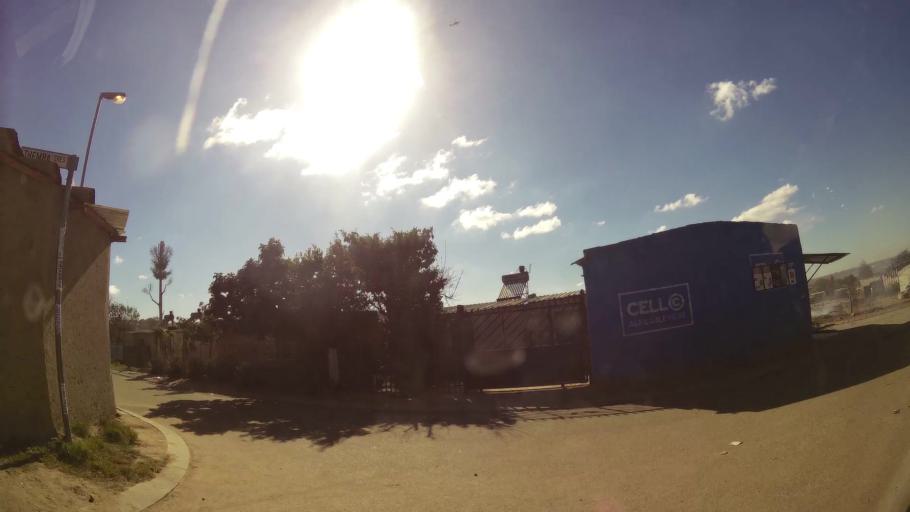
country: ZA
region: Gauteng
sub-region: City of Johannesburg Metropolitan Municipality
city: Diepsloot
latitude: -25.9126
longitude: 28.0927
